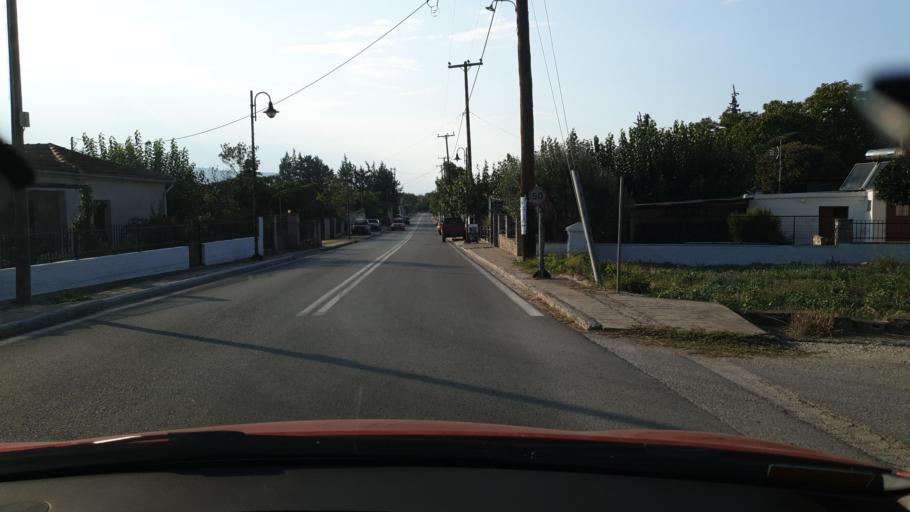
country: GR
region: Thessaly
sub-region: Nomos Magnisias
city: Sourpi
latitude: 39.0986
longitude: 22.8982
